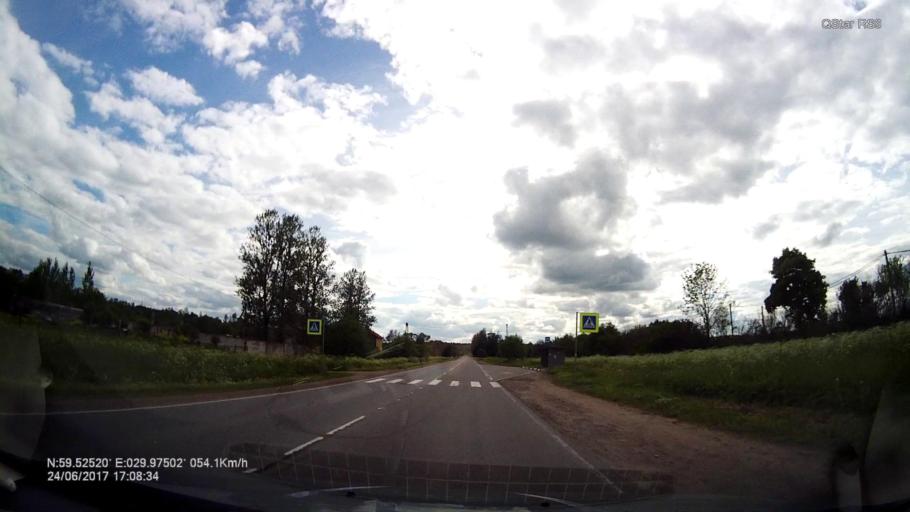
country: RU
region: Leningrad
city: Voyskovitsy
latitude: 59.5250
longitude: 29.9745
